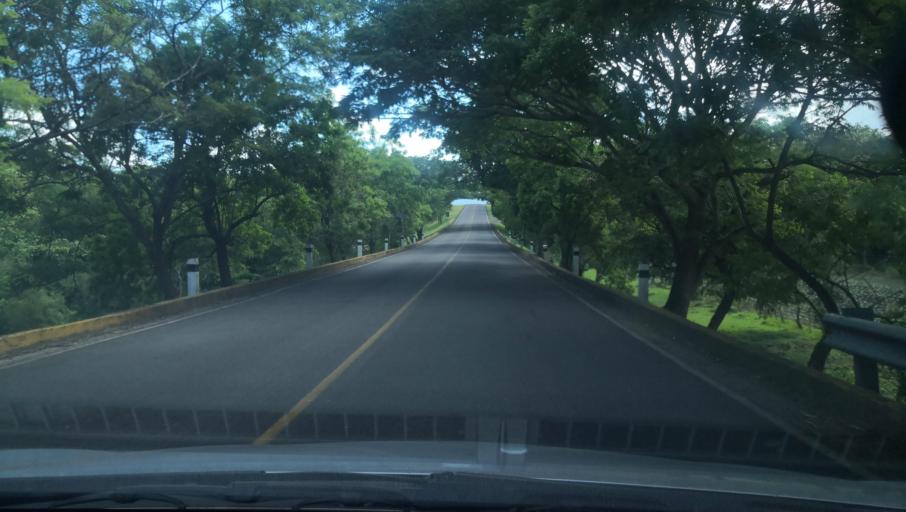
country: NI
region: Madriz
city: Somoto
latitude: 13.4640
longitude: -86.6583
